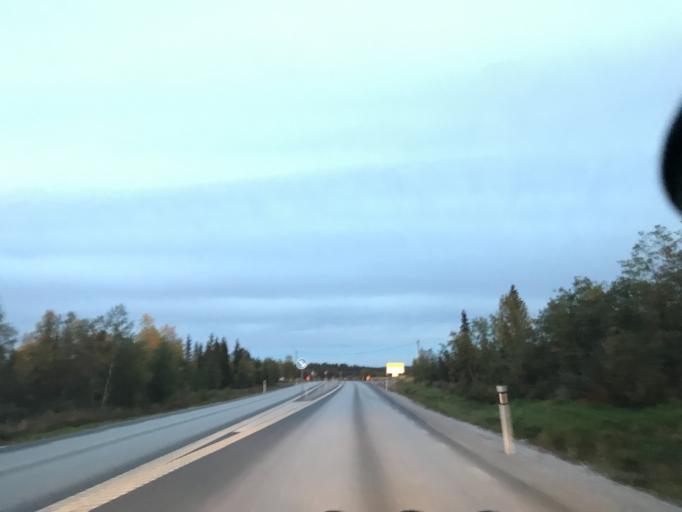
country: SE
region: Norrbotten
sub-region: Gallivare Kommun
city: Malmberget
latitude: 67.6458
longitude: 21.0367
